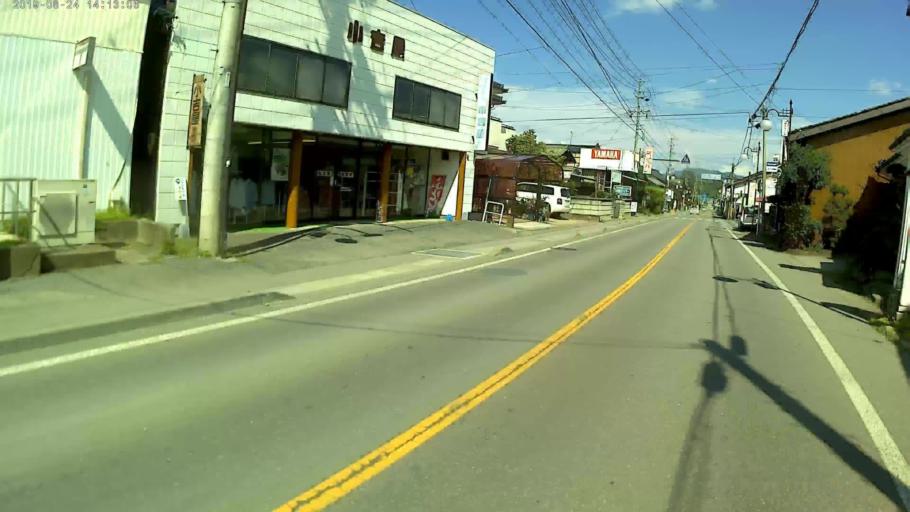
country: JP
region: Nagano
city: Komoro
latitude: 36.2711
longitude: 138.4210
